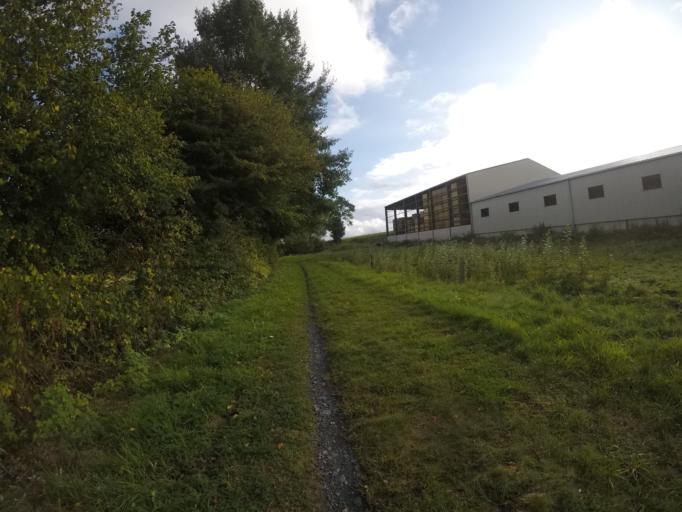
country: BE
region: Wallonia
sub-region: Province du Luxembourg
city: Bastogne
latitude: 49.9514
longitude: 5.6942
